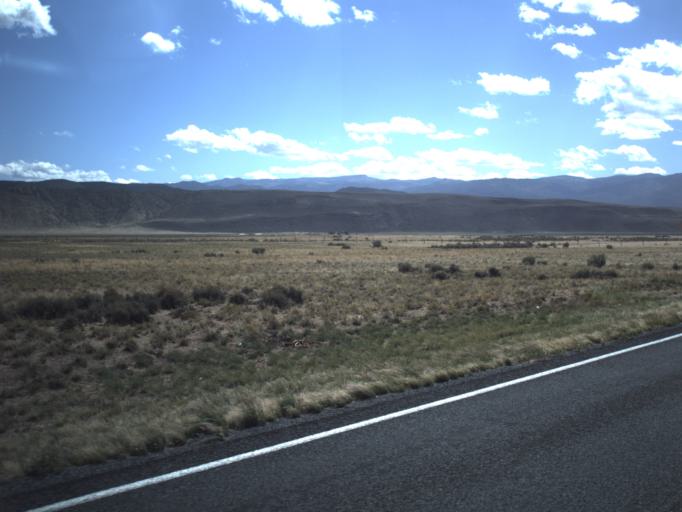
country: US
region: Utah
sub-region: Iron County
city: Enoch
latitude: 37.9054
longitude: -113.0316
